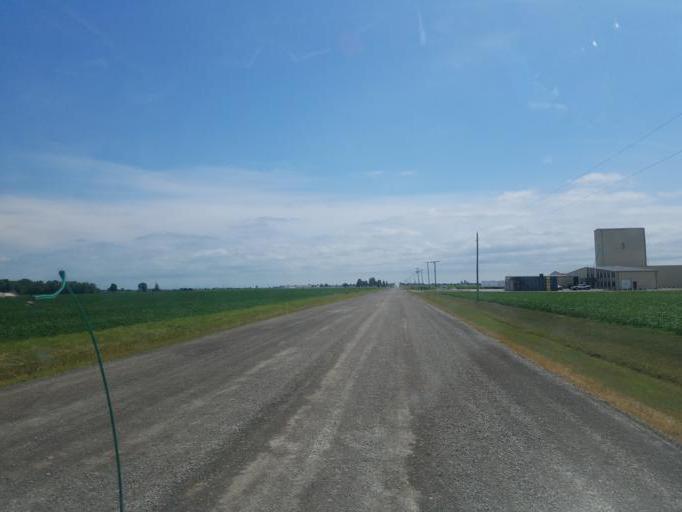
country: US
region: Indiana
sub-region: Allen County
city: Woodburn
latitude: 41.1628
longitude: -84.8489
